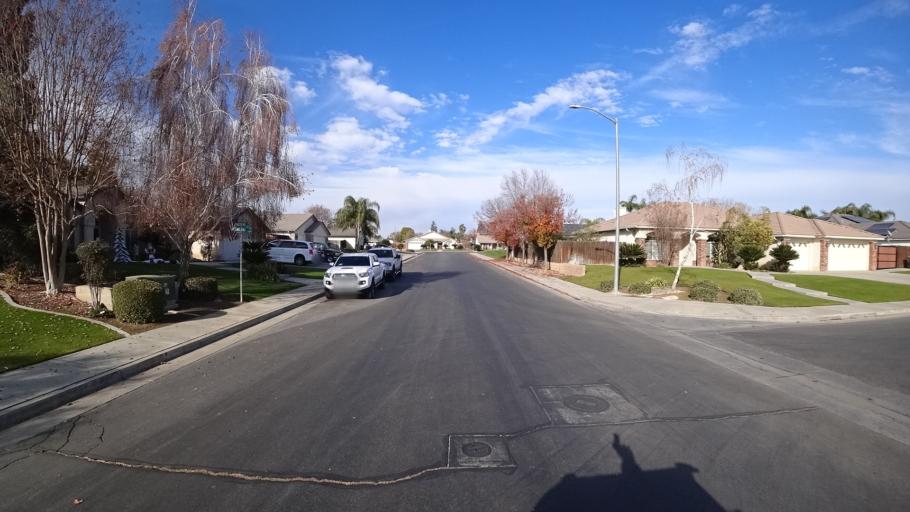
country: US
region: California
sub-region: Kern County
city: Greenacres
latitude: 35.4038
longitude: -119.1161
